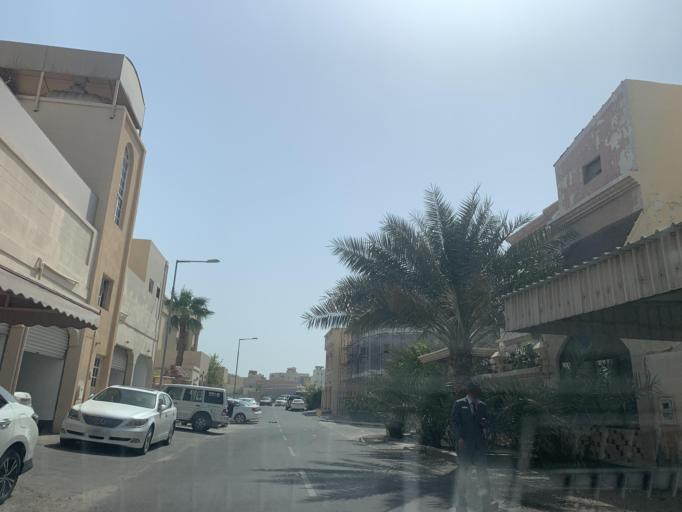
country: BH
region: Northern
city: Madinat `Isa
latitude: 26.1867
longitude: 50.5456
